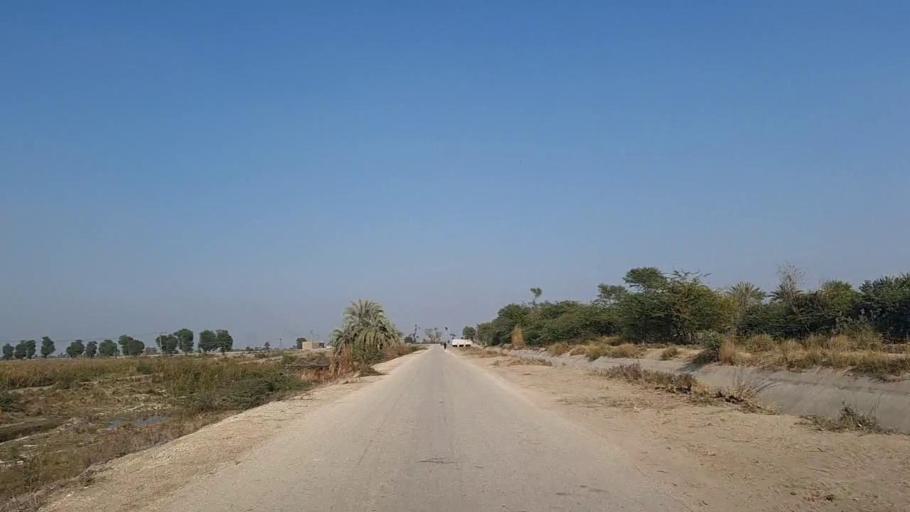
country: PK
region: Sindh
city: Daur
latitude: 26.4548
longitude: 68.2934
